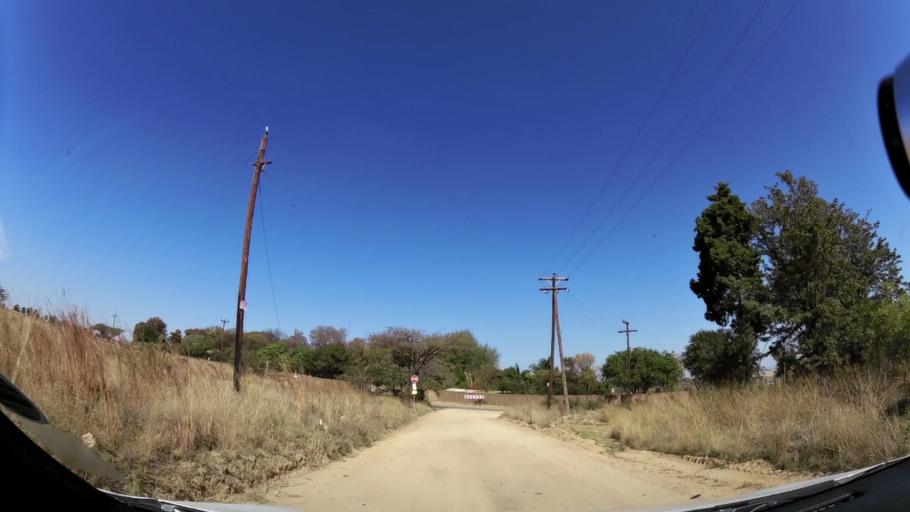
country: ZA
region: Gauteng
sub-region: City of Johannesburg Metropolitan Municipality
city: Diepsloot
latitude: -25.9179
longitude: 28.0703
